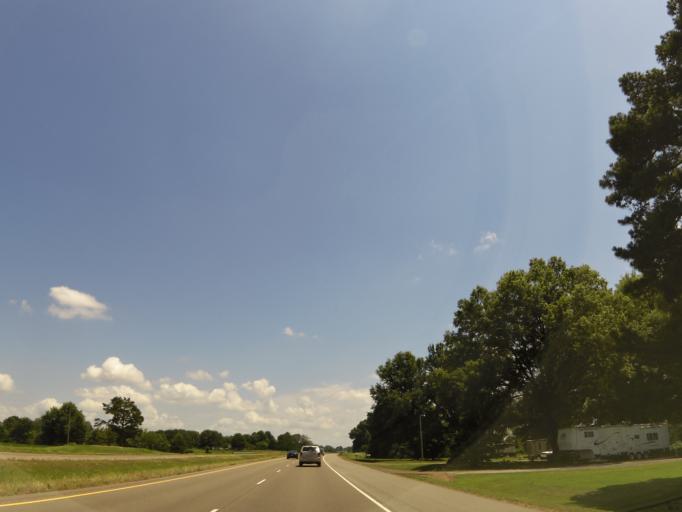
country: US
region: Tennessee
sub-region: Crockett County
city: Alamo
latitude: 35.8513
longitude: -89.1966
